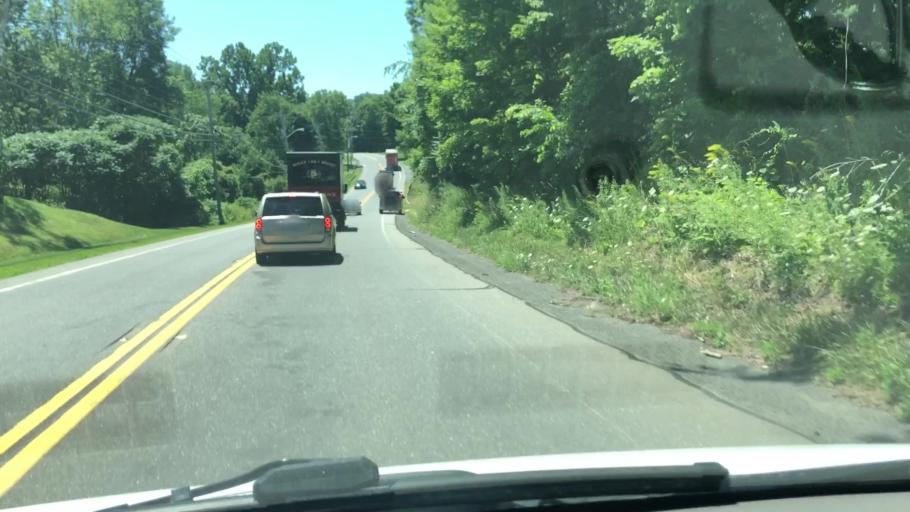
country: US
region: Massachusetts
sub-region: Berkshire County
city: Adams
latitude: 42.5792
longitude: -73.1491
